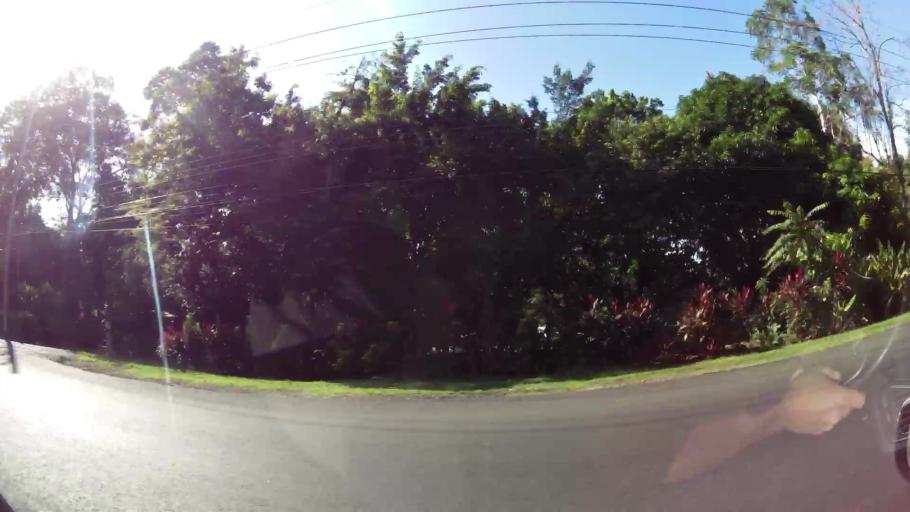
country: CR
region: Puntarenas
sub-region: Canton de Garabito
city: Jaco
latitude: 9.5975
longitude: -84.6185
